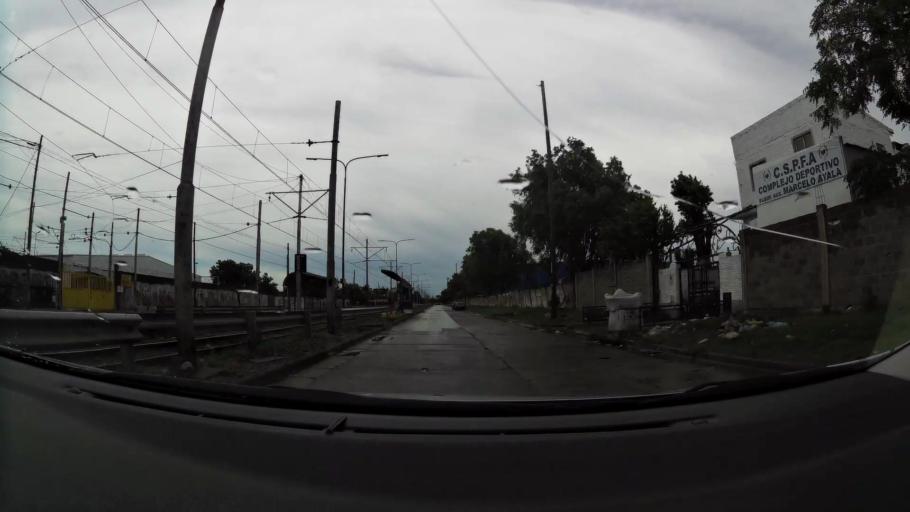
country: AR
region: Buenos Aires F.D.
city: Villa Lugano
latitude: -34.6565
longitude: -58.4536
